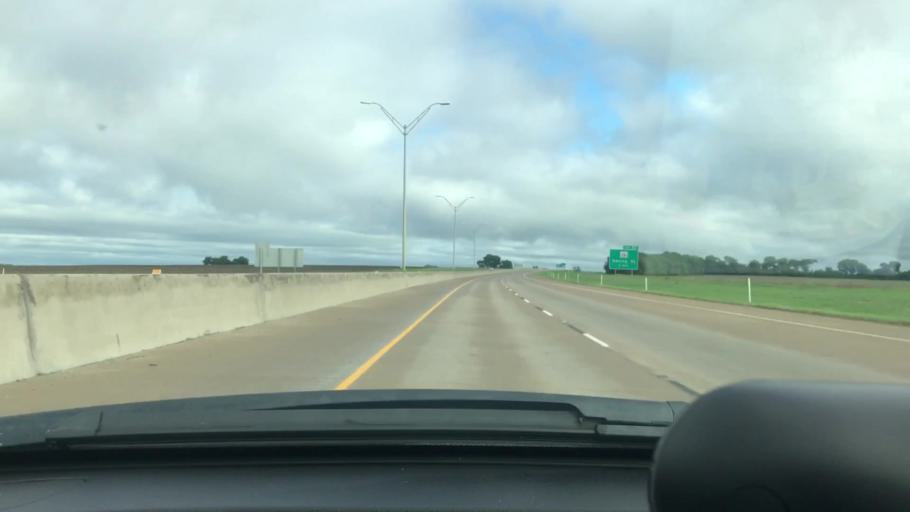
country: US
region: Texas
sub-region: Grayson County
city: Howe
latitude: 33.4738
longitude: -96.6174
